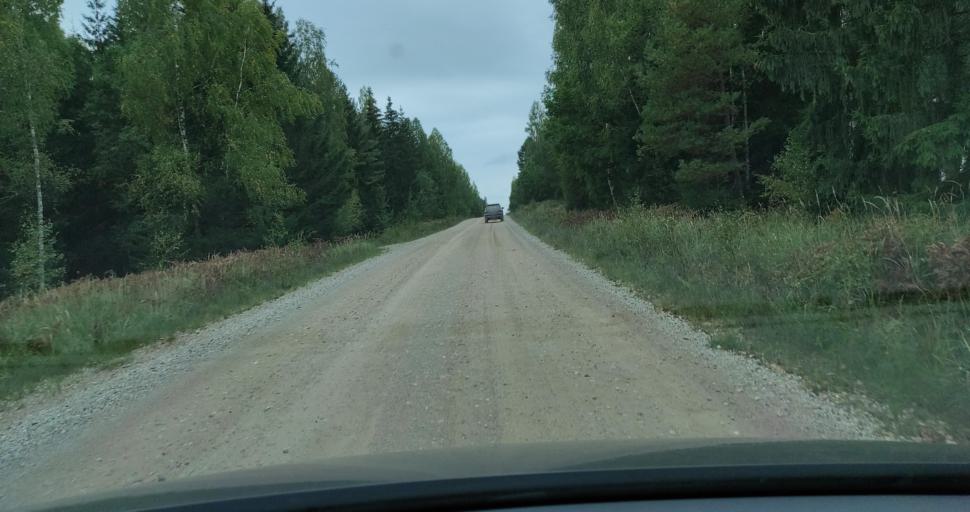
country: LV
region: Talsu Rajons
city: Stende
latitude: 57.0835
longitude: 22.2573
